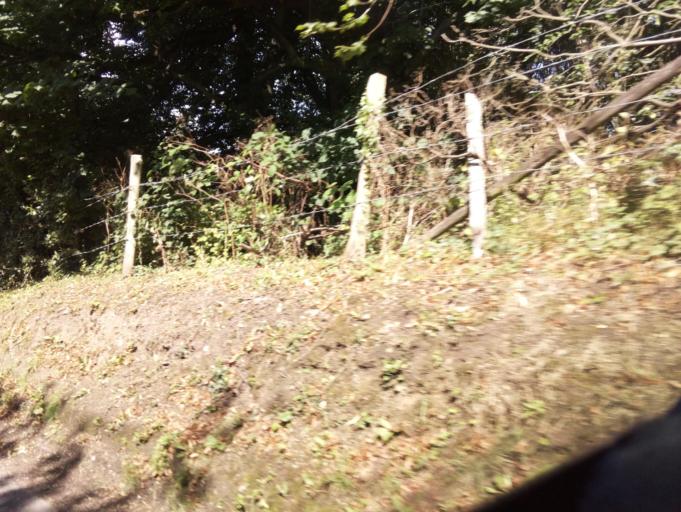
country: GB
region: England
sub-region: West Berkshire
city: Greenham
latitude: 51.3568
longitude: -1.2819
